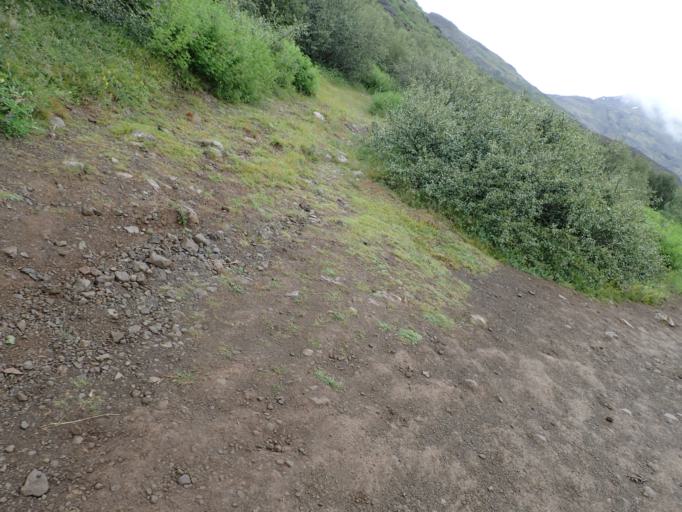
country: IS
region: South
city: Hveragerdi
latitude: 64.3852
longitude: -21.2888
